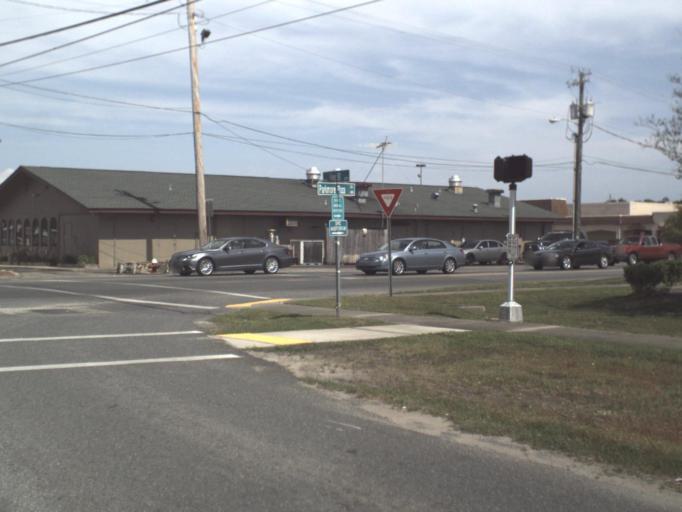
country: US
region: Florida
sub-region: Santa Rosa County
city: Bagdad
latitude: 30.6053
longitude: -87.0657
